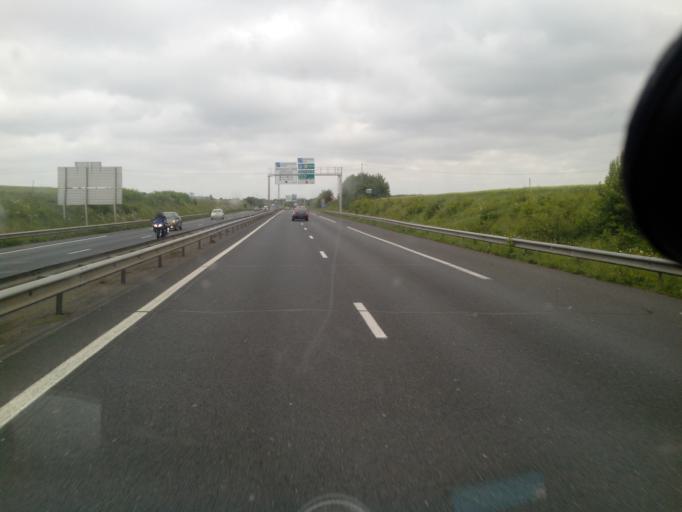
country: FR
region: Lower Normandy
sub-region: Departement du Calvados
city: Verson
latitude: 49.1640
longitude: -0.4389
